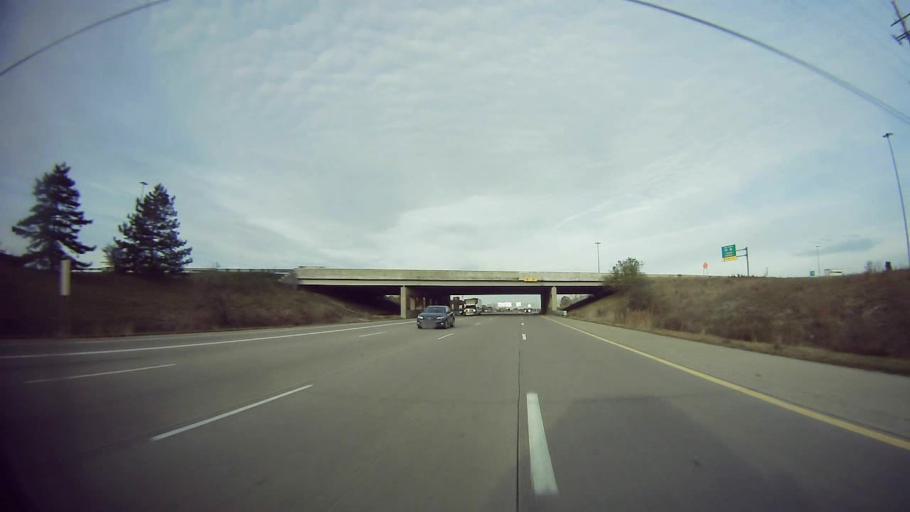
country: US
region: Michigan
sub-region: Oakland County
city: Bingham Farms
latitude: 42.4880
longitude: -83.2839
